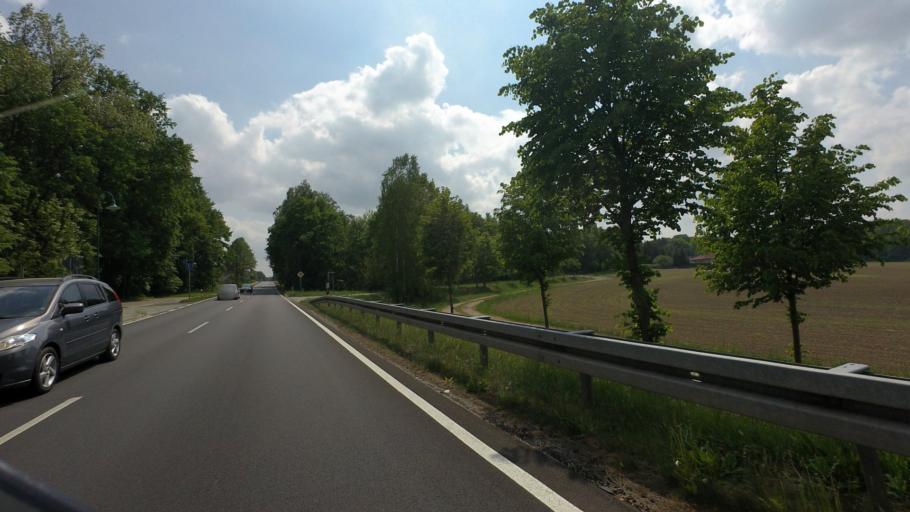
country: DE
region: Saxony
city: Rietschen
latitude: 51.3550
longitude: 14.8021
